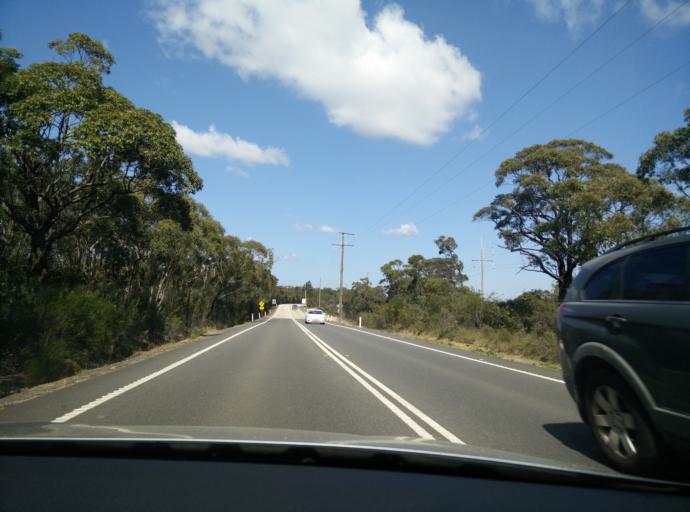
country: AU
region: New South Wales
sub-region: Gosford Shire
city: Point Clare
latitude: -33.4562
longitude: 151.2856
